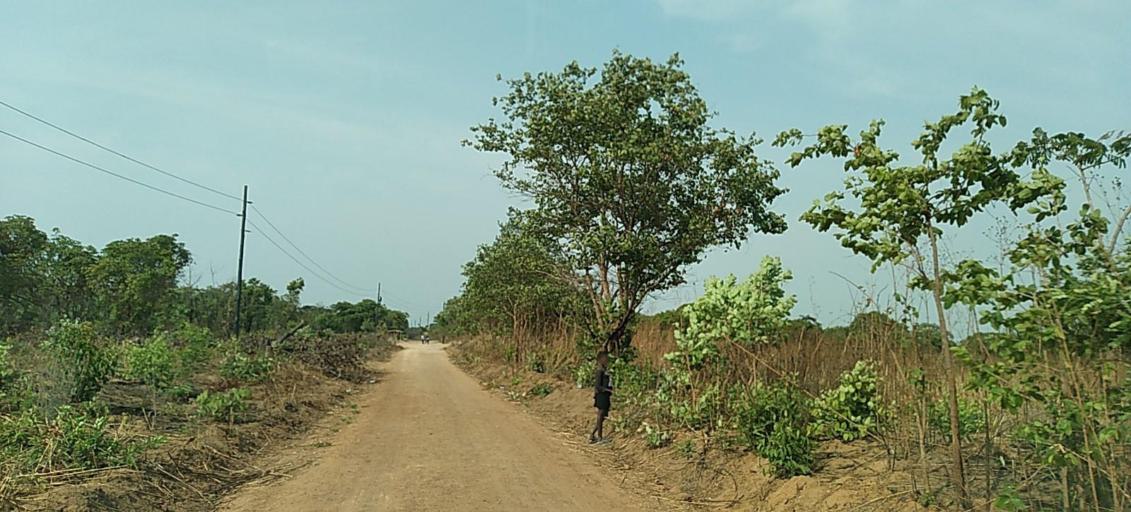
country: ZM
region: Copperbelt
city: Ndola
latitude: -13.2223
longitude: 28.6770
